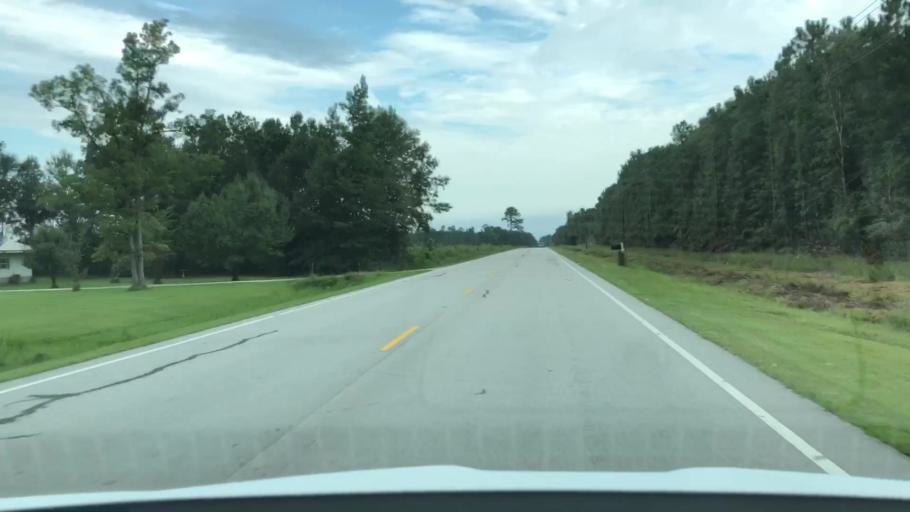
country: US
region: North Carolina
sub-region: Lenoir County
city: Kinston
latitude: 35.1248
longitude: -77.5199
